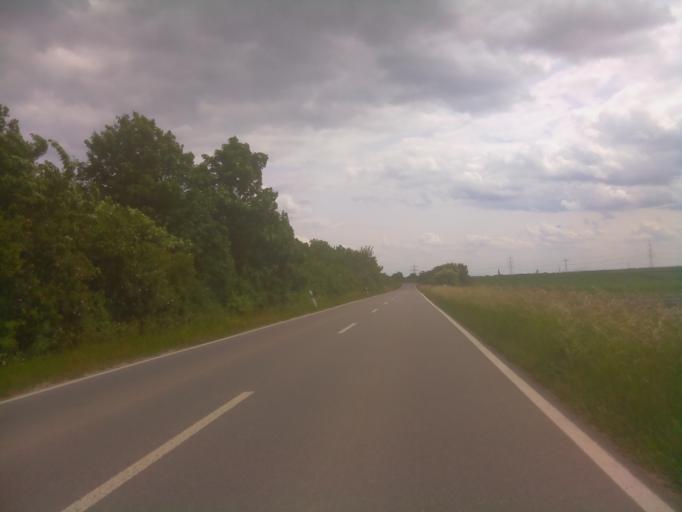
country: DE
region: Rheinland-Pfalz
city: Gerolsheim
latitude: 49.5426
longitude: 8.2740
